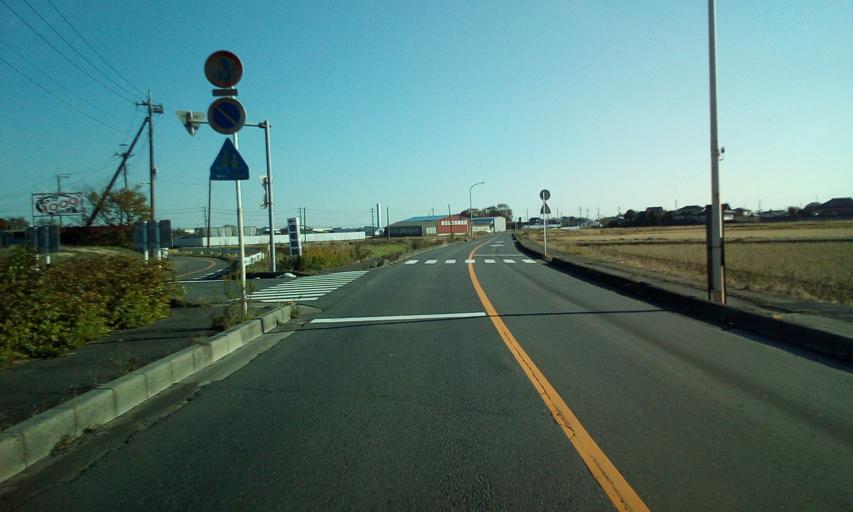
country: JP
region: Saitama
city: Yoshikawa
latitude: 35.8942
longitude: 139.8783
